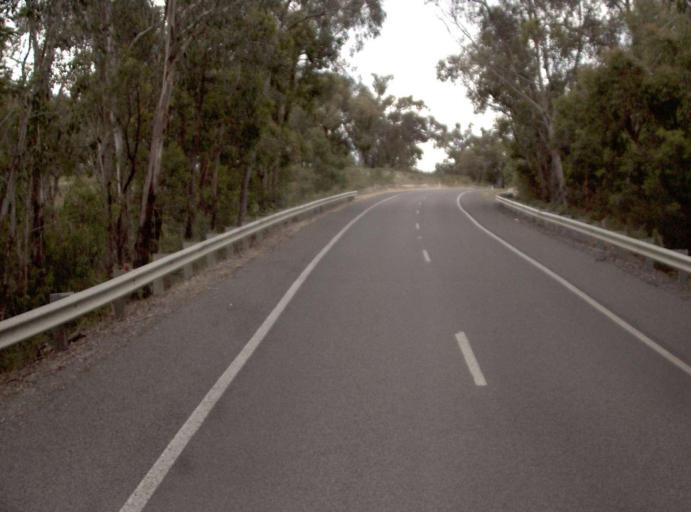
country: AU
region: Victoria
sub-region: Wellington
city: Sale
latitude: -38.3272
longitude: 147.0182
